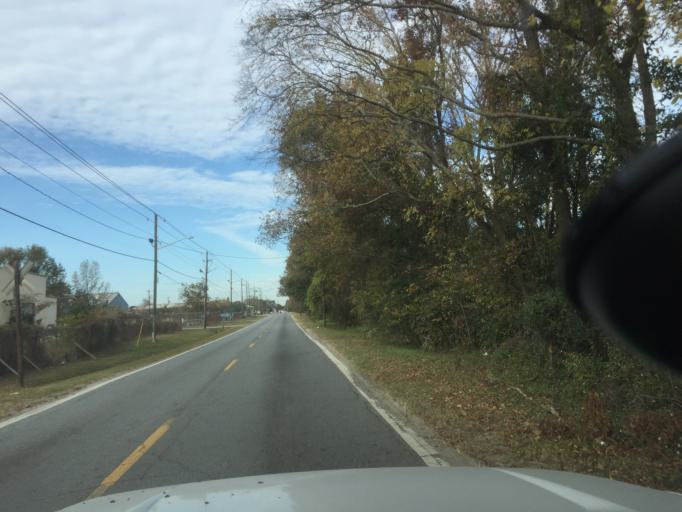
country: US
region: Georgia
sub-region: Chatham County
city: Savannah
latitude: 32.0813
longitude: -81.1200
